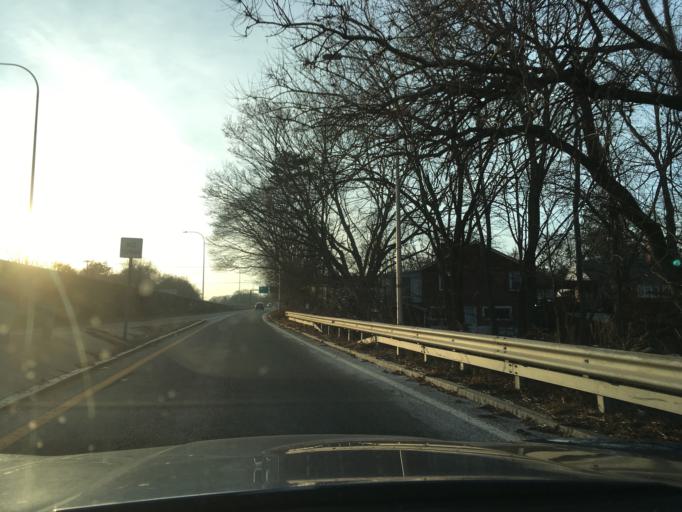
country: US
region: Rhode Island
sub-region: Providence County
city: North Providence
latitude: 41.8219
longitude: -71.4729
